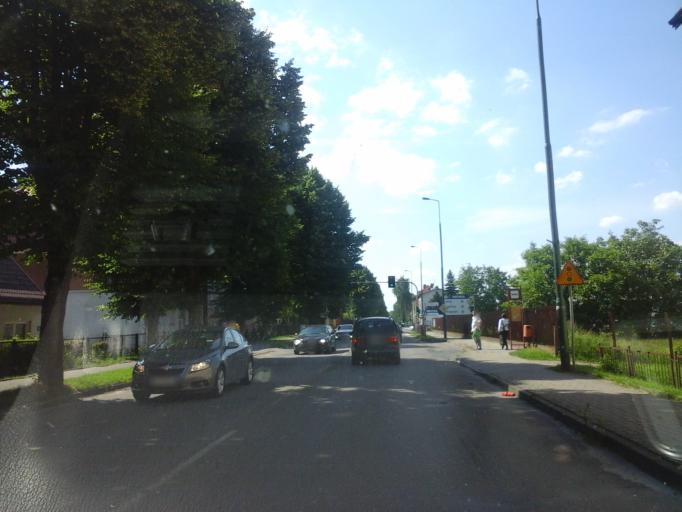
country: PL
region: West Pomeranian Voivodeship
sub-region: Powiat bialogardzki
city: Bialogard
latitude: 54.0084
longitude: 15.9728
